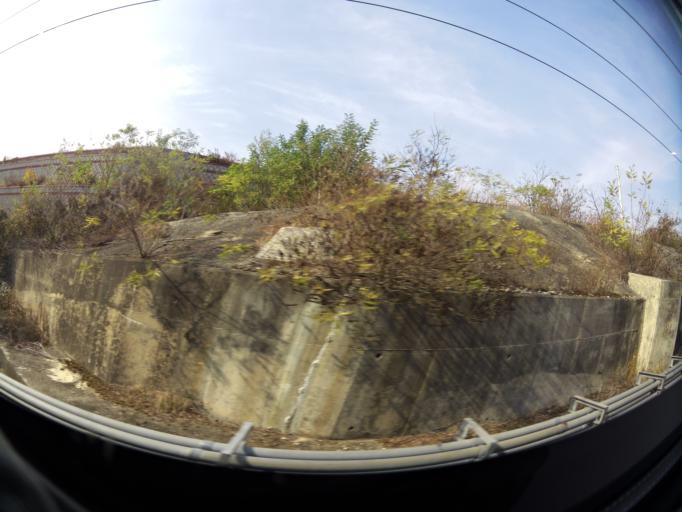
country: KR
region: Gyeongsangbuk-do
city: Gimcheon
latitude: 36.1959
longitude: 128.0050
